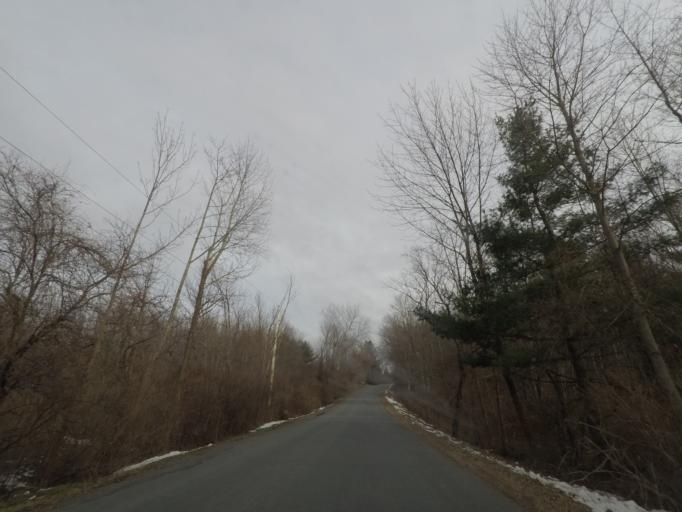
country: US
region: New York
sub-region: Rensselaer County
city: West Sand Lake
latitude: 42.6430
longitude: -73.6408
